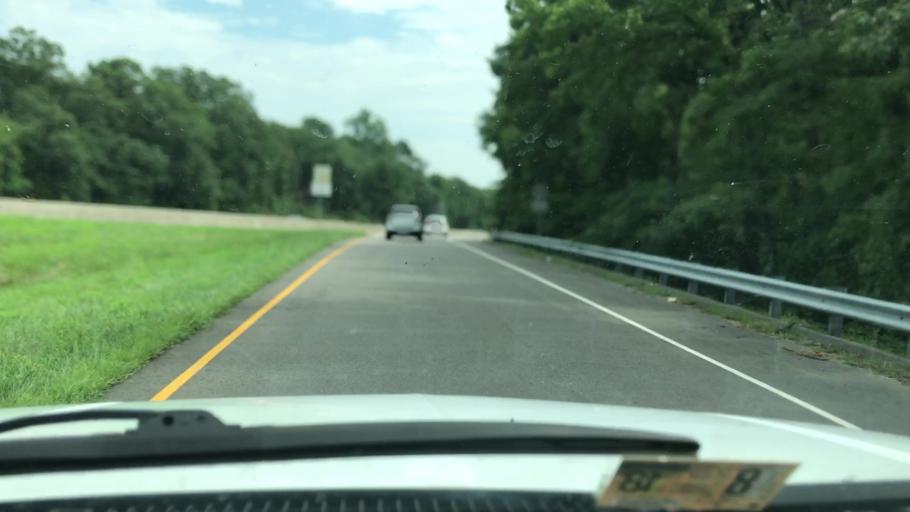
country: US
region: Virginia
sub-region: Chesterfield County
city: Bon Air
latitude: 37.4993
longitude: -77.5244
